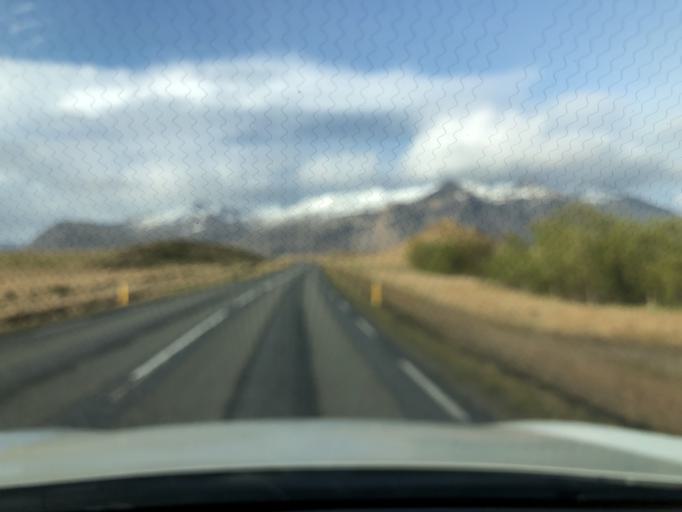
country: IS
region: East
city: Hoefn
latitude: 64.2780
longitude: -15.1975
